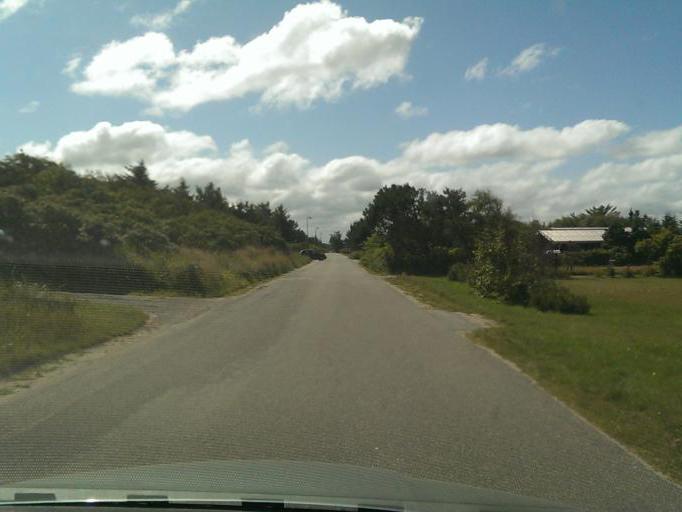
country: DK
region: North Denmark
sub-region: Jammerbugt Kommune
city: Pandrup
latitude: 57.2544
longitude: 9.5939
